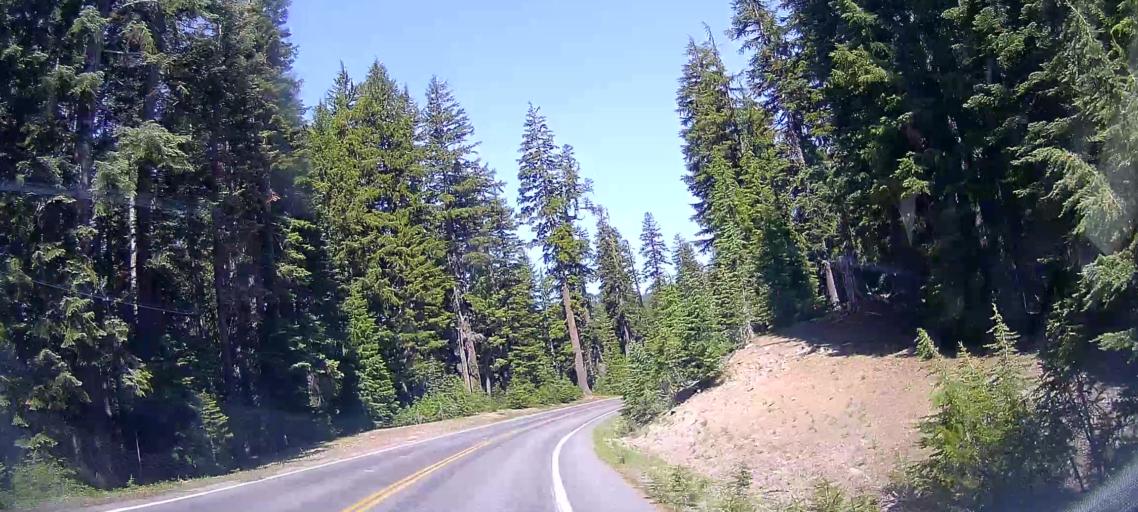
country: US
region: Oregon
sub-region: Jackson County
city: Shady Cove
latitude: 42.8817
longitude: -122.1279
